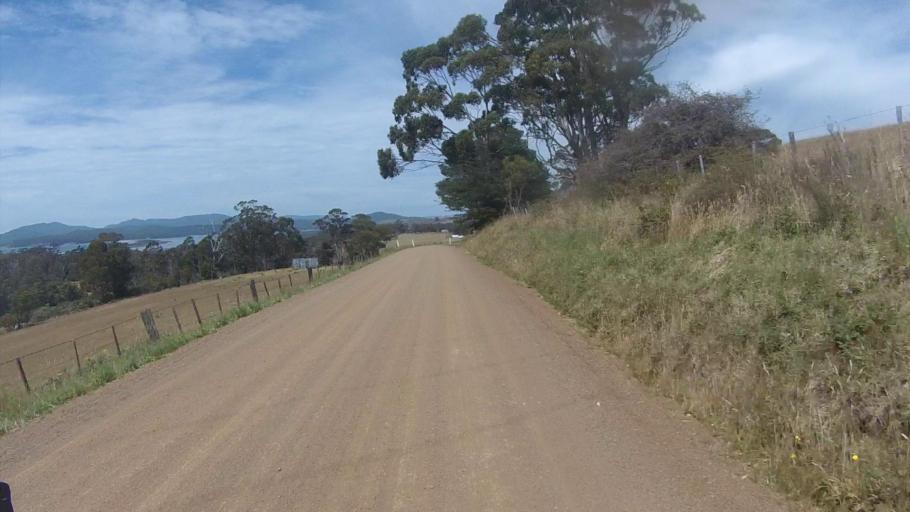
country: AU
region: Tasmania
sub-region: Sorell
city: Sorell
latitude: -42.7942
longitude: 147.8418
